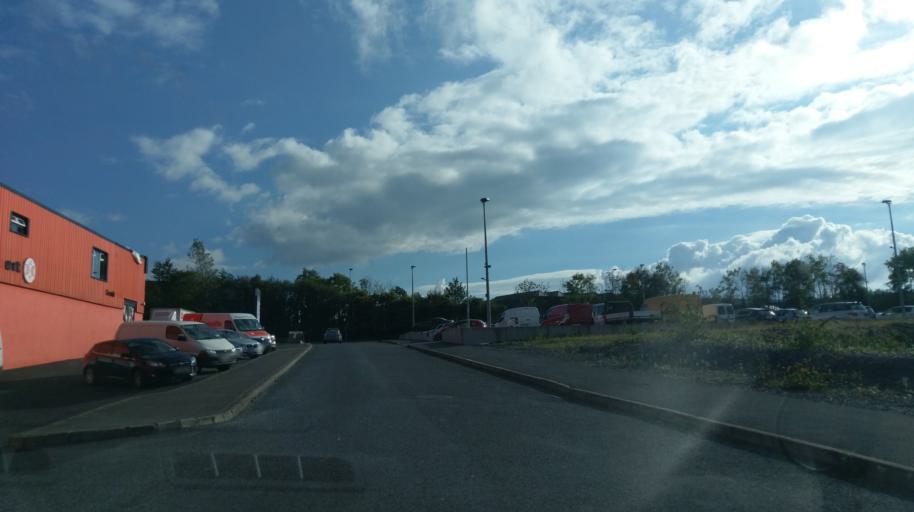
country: IE
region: Connaught
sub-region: County Galway
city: Gaillimh
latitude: 53.2890
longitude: -9.0255
